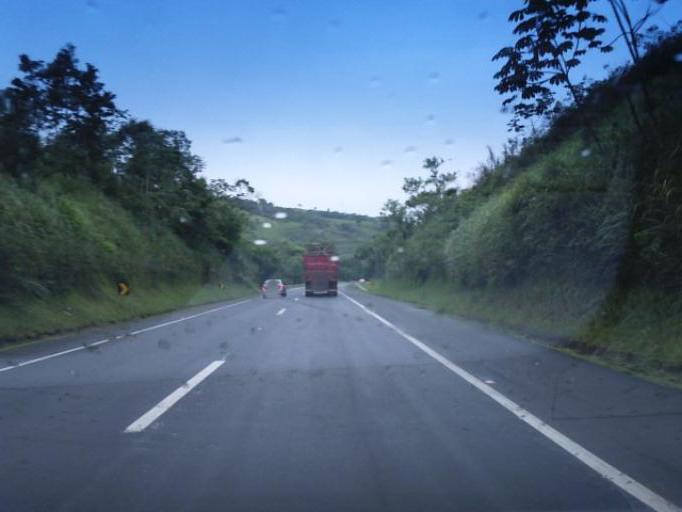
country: BR
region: Sao Paulo
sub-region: Cajati
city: Cajati
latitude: -24.7798
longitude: -48.2027
